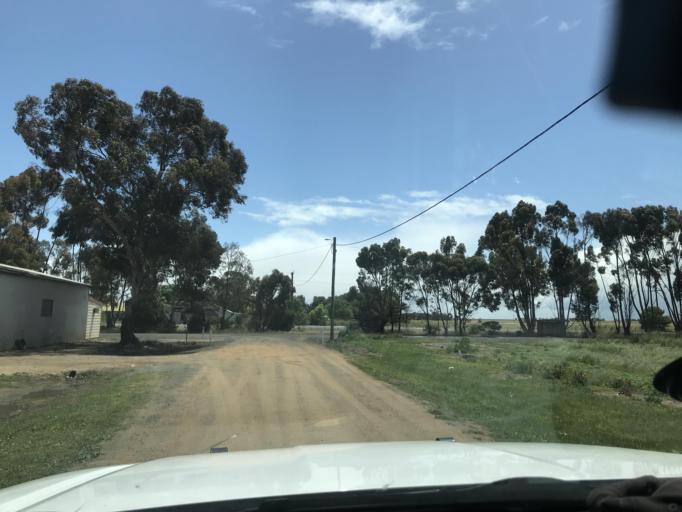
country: AU
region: South Australia
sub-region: Tatiara
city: Bordertown
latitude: -36.3630
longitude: 141.1294
